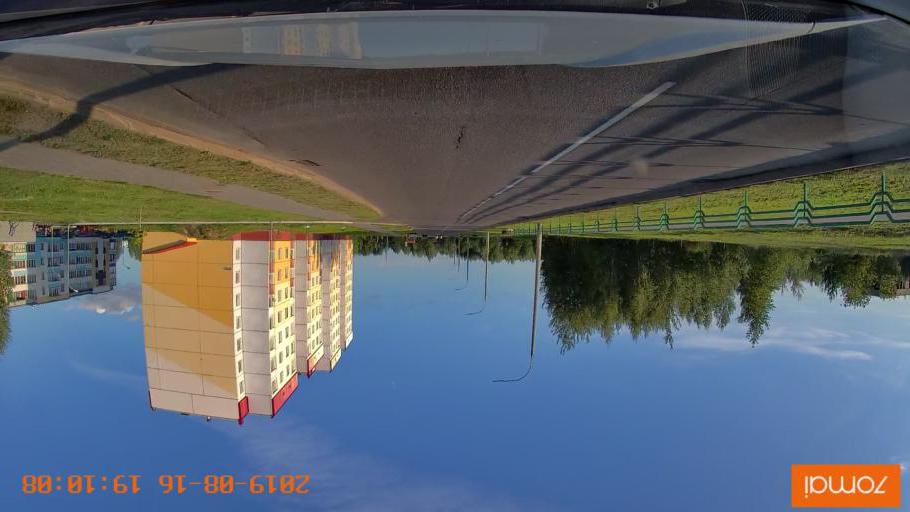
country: BY
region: Mogilev
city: Asipovichy
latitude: 53.3229
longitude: 28.6386
